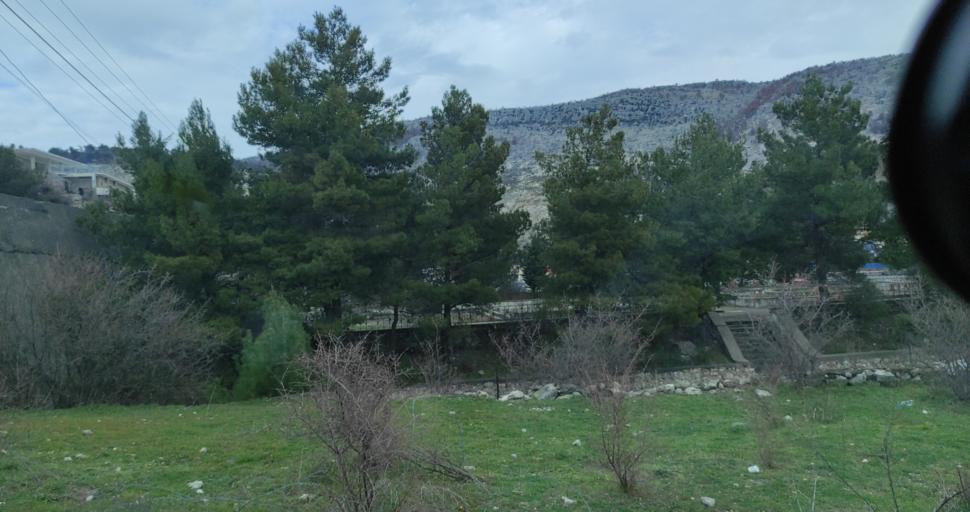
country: AL
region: Lezhe
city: Shengjin
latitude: 41.8113
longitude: 19.5849
